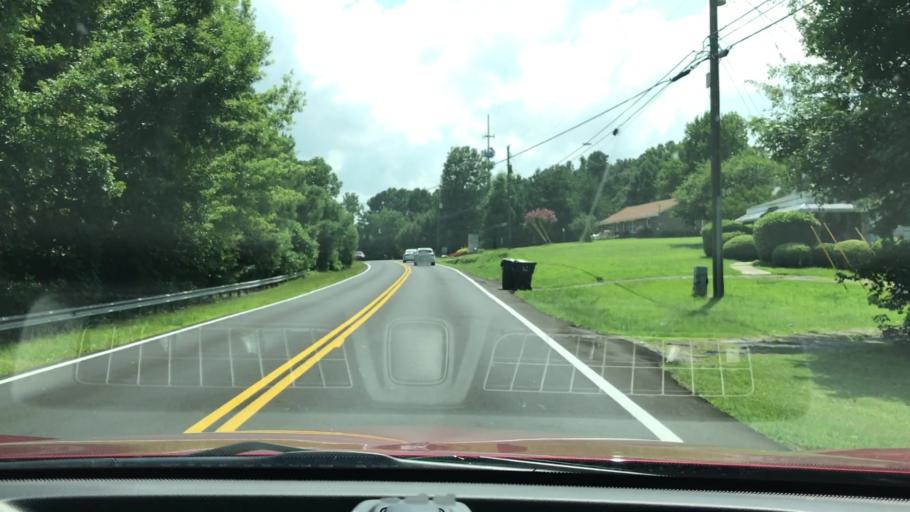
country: US
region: Georgia
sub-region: Gwinnett County
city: Buford
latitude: 34.0694
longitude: -83.9871
